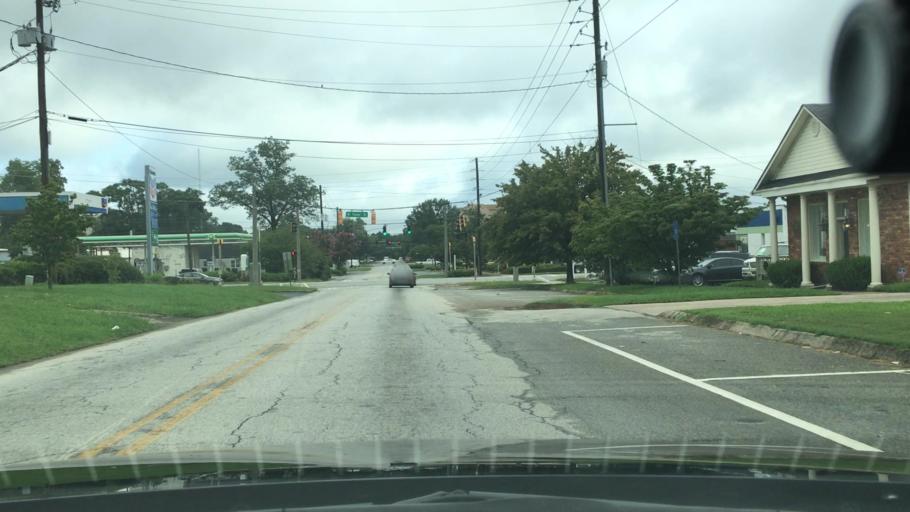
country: US
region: Georgia
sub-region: Spalding County
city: Griffin
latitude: 33.2464
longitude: -84.2688
